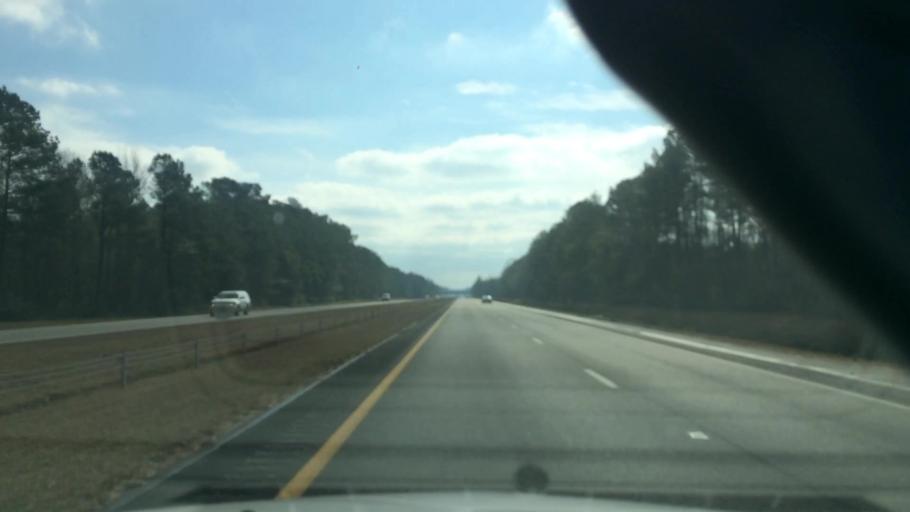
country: US
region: North Carolina
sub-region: Pender County
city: Rocky Point
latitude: 34.4919
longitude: -77.8776
